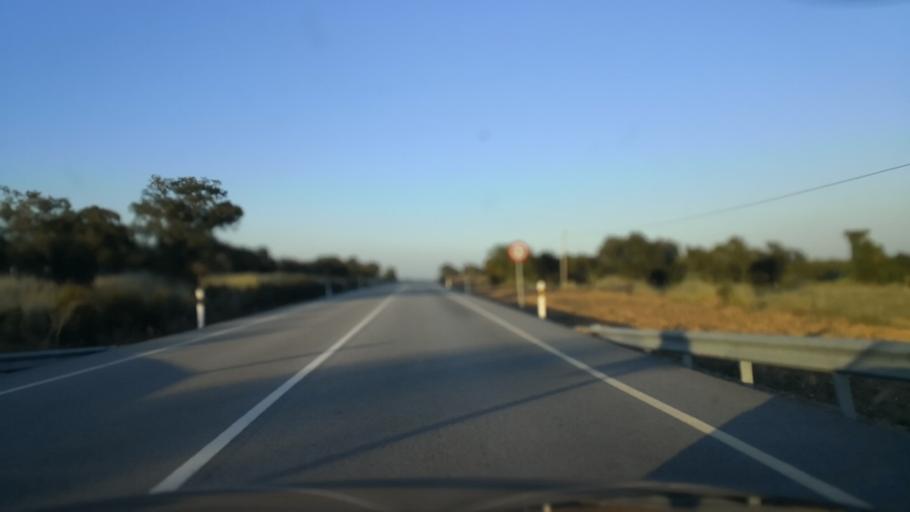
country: ES
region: Extremadura
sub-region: Provincia de Caceres
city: Salorino
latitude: 39.5081
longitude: -7.1189
